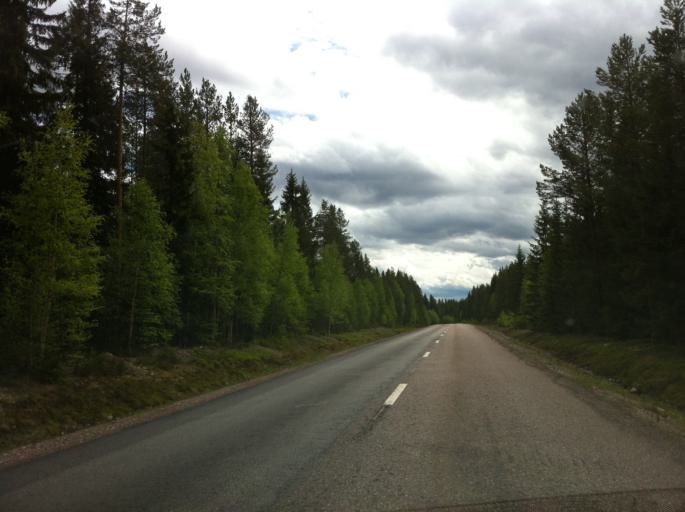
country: NO
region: Hedmark
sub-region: Trysil
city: Innbygda
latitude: 61.5245
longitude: 13.0790
